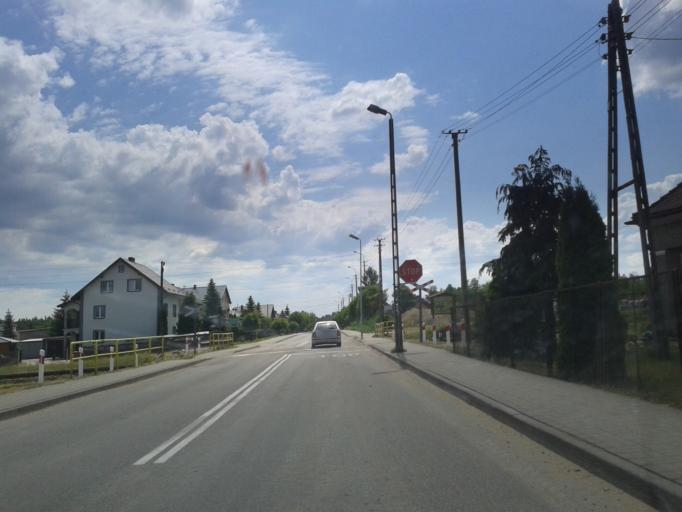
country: PL
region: Pomeranian Voivodeship
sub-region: Powiat koscierski
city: Karsin
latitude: 53.8981
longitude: 17.9345
